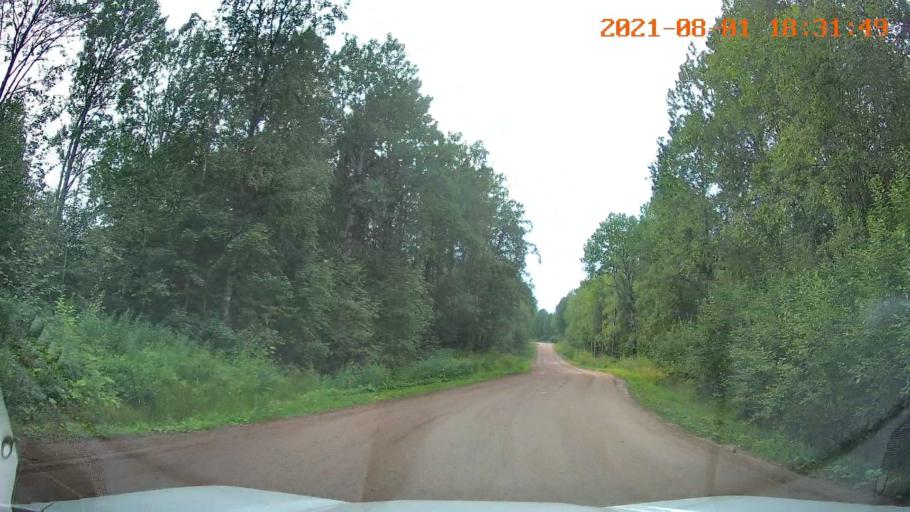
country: RU
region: Leningrad
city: Voznesen'ye
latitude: 60.8899
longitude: 35.3349
